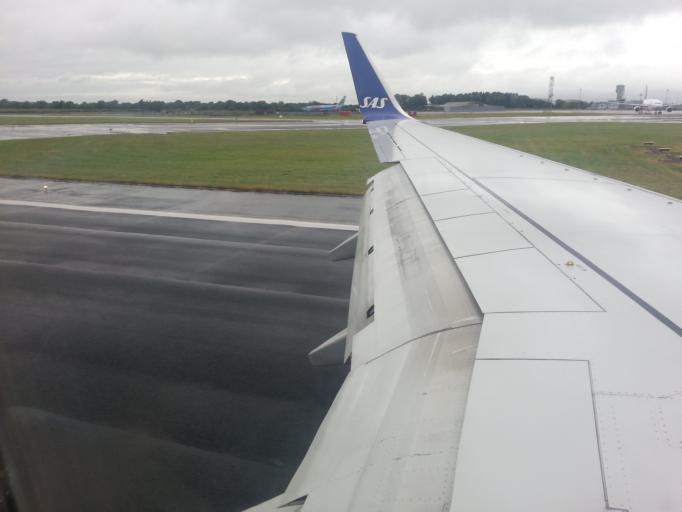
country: IE
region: Leinster
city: Ballymun
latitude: 53.4211
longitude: -6.2643
